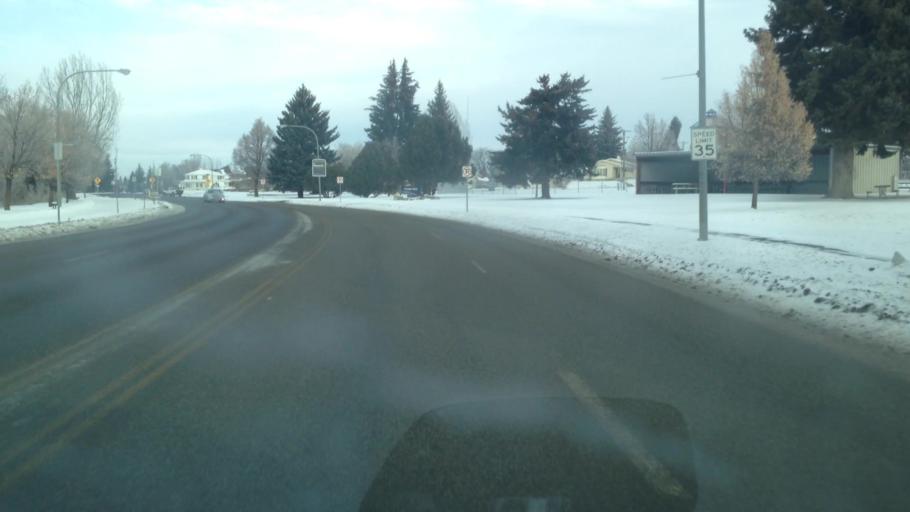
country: US
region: Idaho
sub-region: Bonneville County
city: Idaho Falls
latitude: 43.5023
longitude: -112.0438
